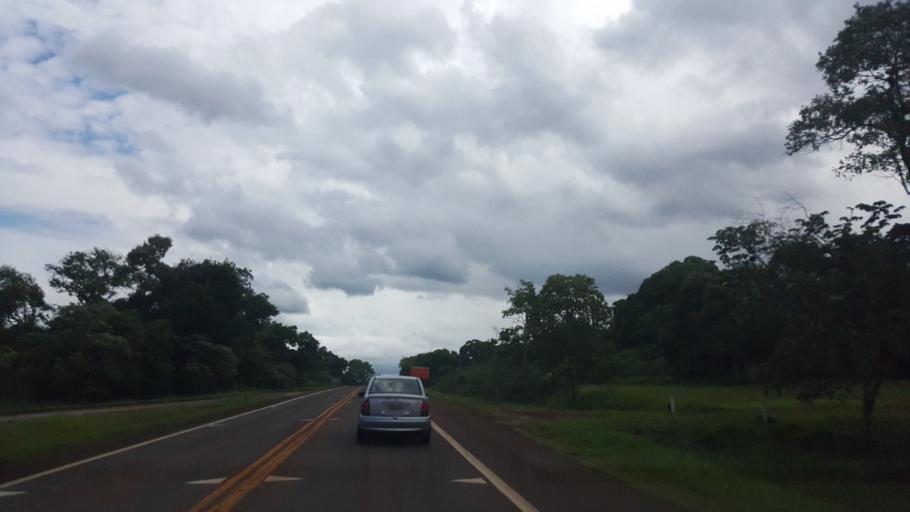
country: AR
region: Misiones
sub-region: Departamento de Iguazu
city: Puerto Iguazu
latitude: -25.7354
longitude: -54.5339
